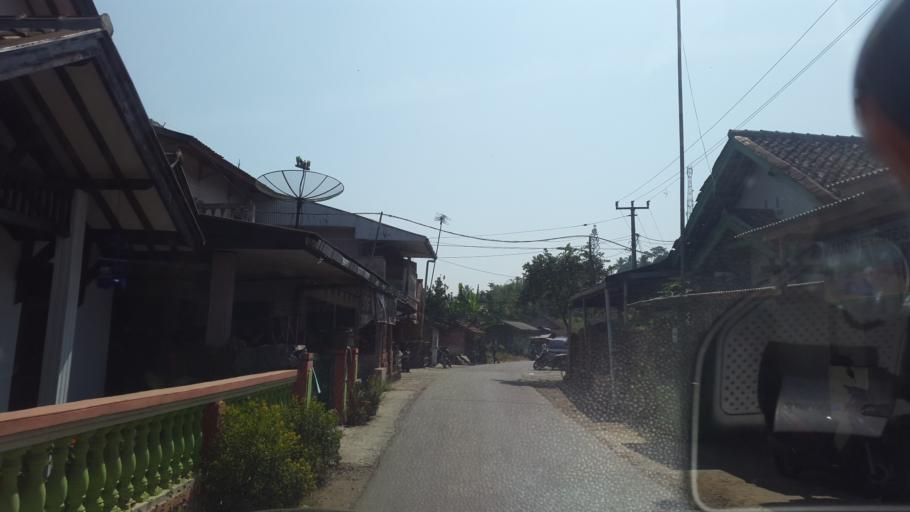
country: ID
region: West Java
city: Cicurug
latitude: -6.8417
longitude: 106.8261
